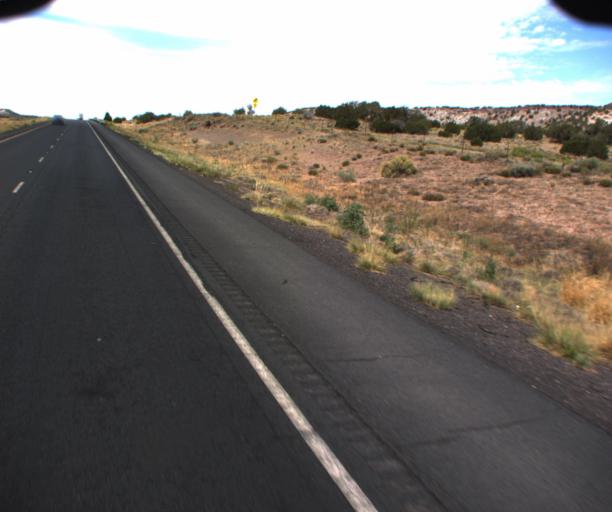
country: US
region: Arizona
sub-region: Apache County
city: Houck
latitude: 35.3007
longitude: -109.1299
